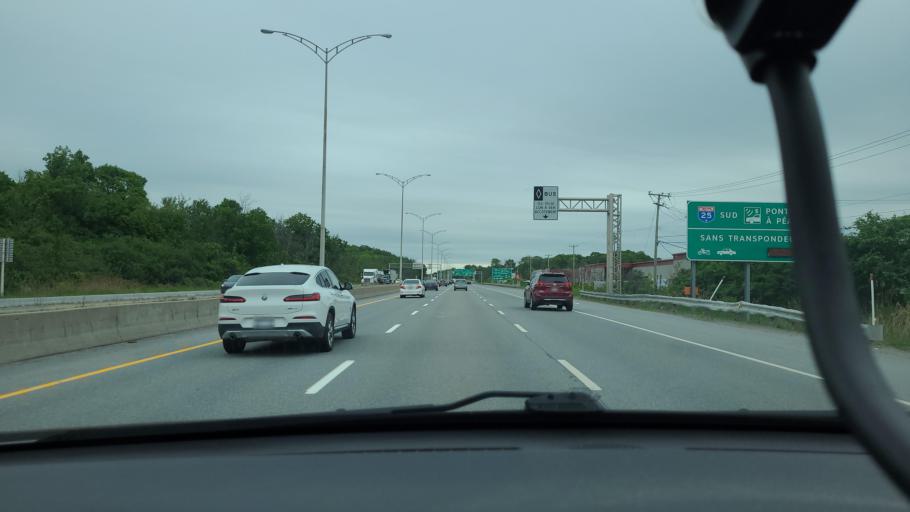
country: CA
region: Quebec
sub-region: Lanaudiere
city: Terrebonne
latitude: 45.6376
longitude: -73.6522
